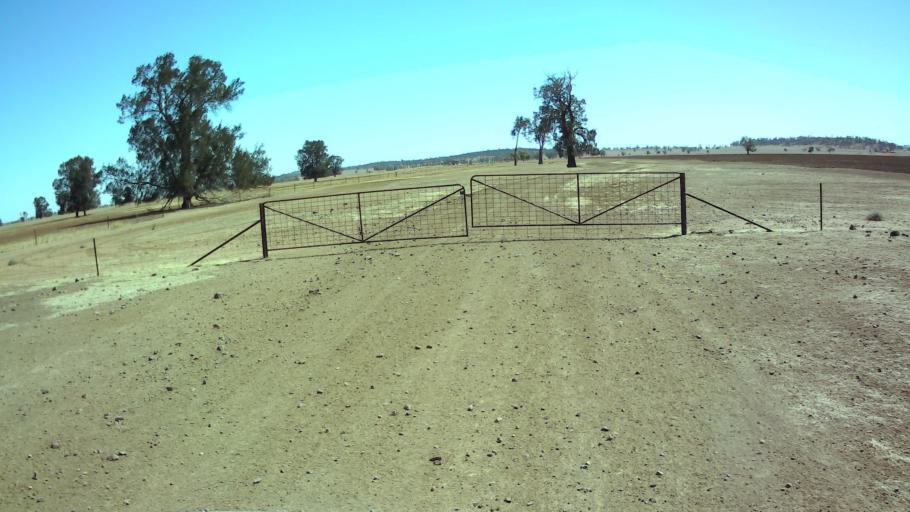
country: AU
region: New South Wales
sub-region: Forbes
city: Forbes
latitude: -33.7120
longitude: 147.6672
